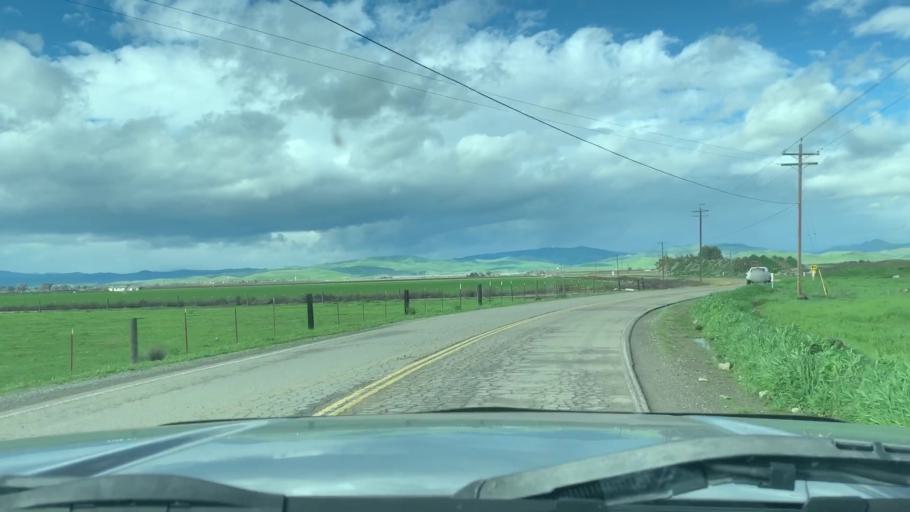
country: US
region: California
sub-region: Merced County
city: Gustine
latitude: 37.1220
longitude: -120.9786
